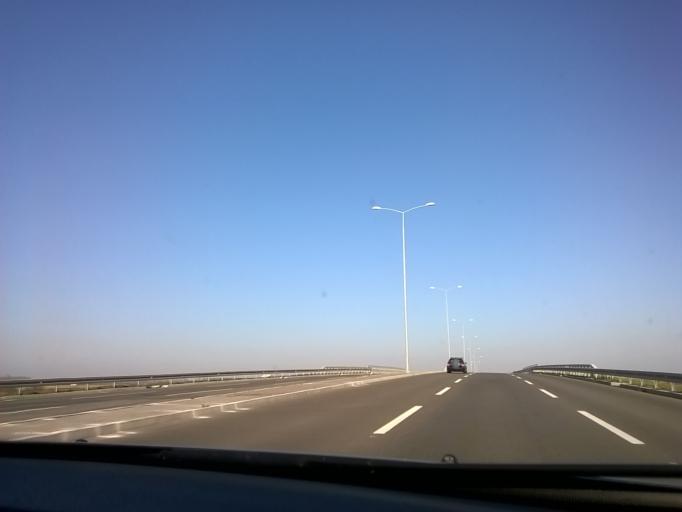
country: RS
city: Ovca
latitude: 44.9064
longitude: 20.5124
